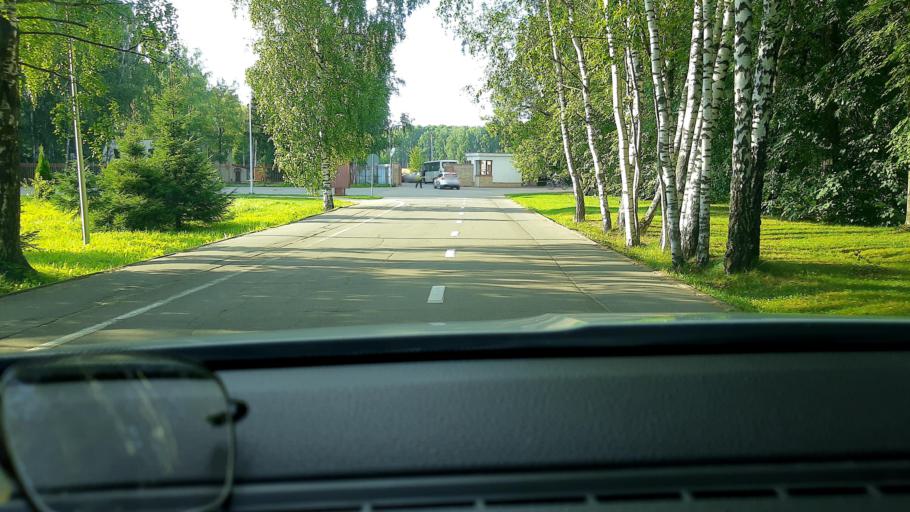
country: RU
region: Moskovskaya
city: Marfino
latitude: 56.0950
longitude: 37.5376
